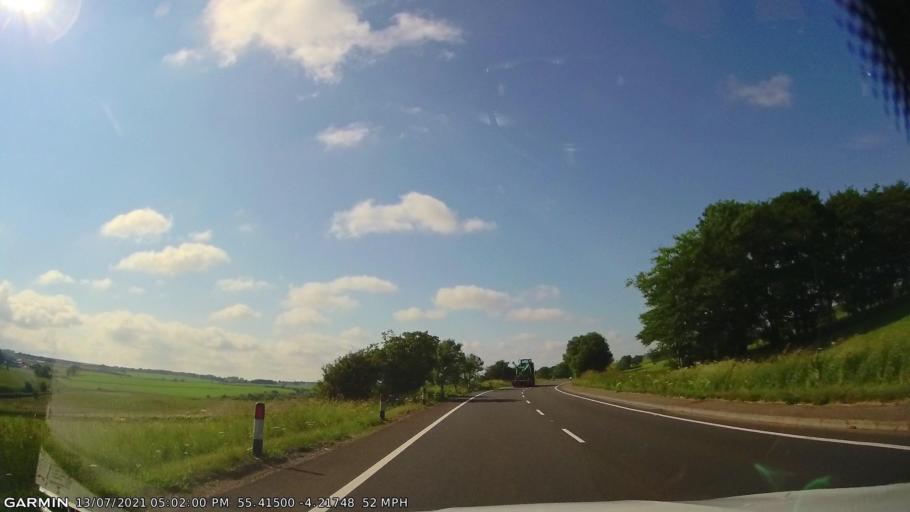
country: GB
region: Scotland
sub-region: East Ayrshire
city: New Cumnock
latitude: 55.4150
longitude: -4.2175
